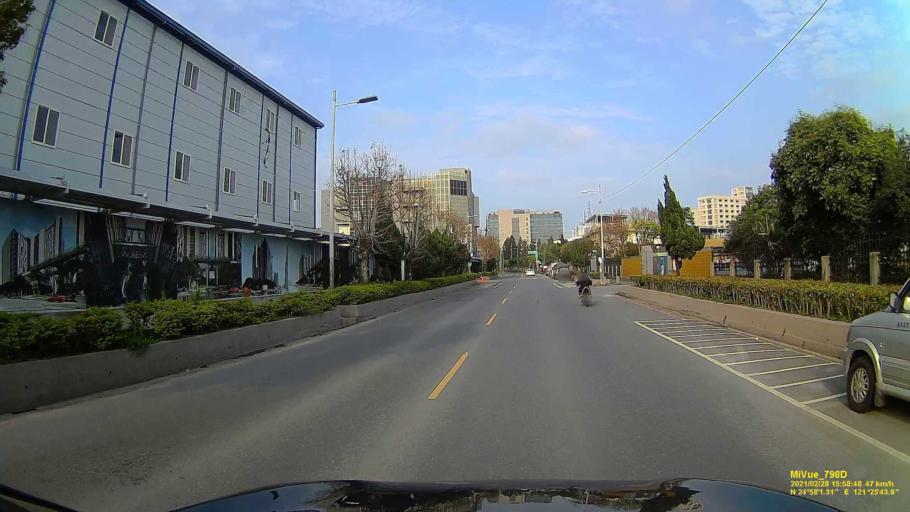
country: TW
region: Taipei
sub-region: Taipei
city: Banqiao
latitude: 24.9671
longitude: 121.4291
